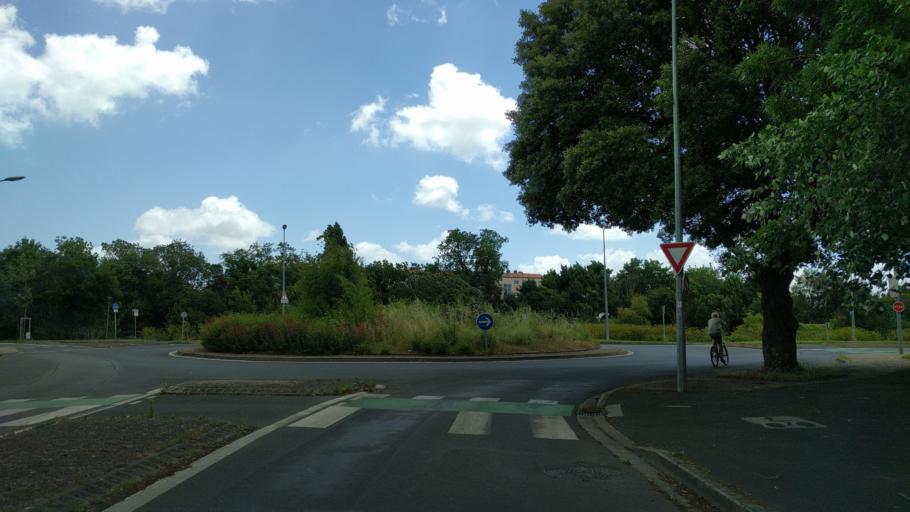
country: FR
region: Poitou-Charentes
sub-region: Departement de la Charente-Maritime
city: La Rochelle
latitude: 46.1607
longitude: -1.1293
